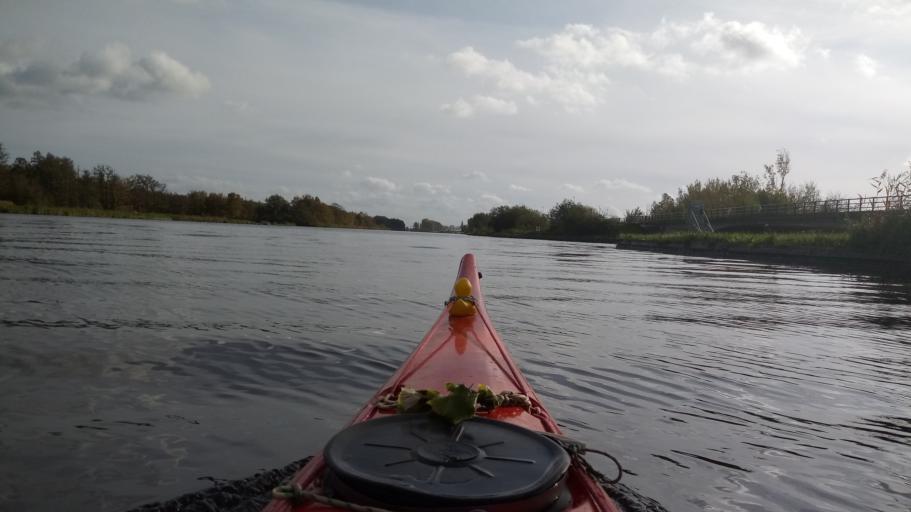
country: NL
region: Overijssel
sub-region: Gemeente Steenwijkerland
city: Wanneperveen
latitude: 52.6771
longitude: 6.0913
